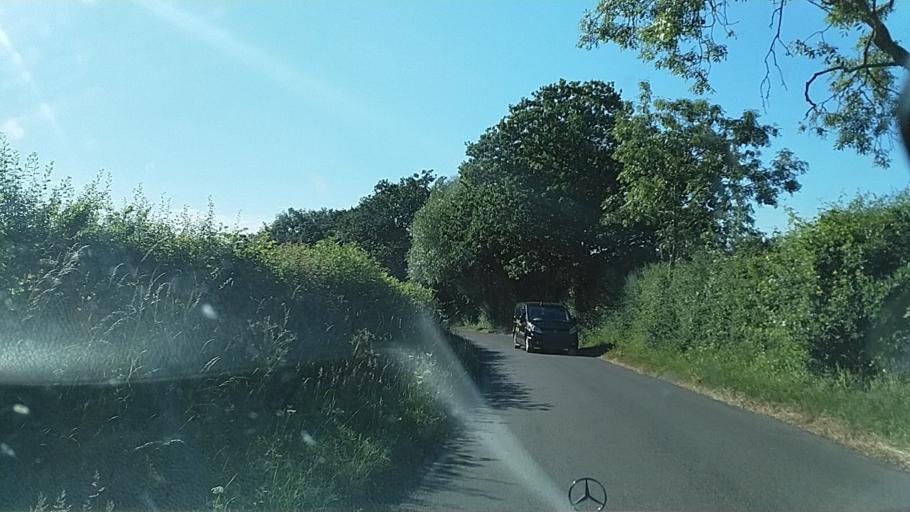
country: GB
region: England
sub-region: Warwickshire
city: Wroxall
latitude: 52.3136
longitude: -1.6403
